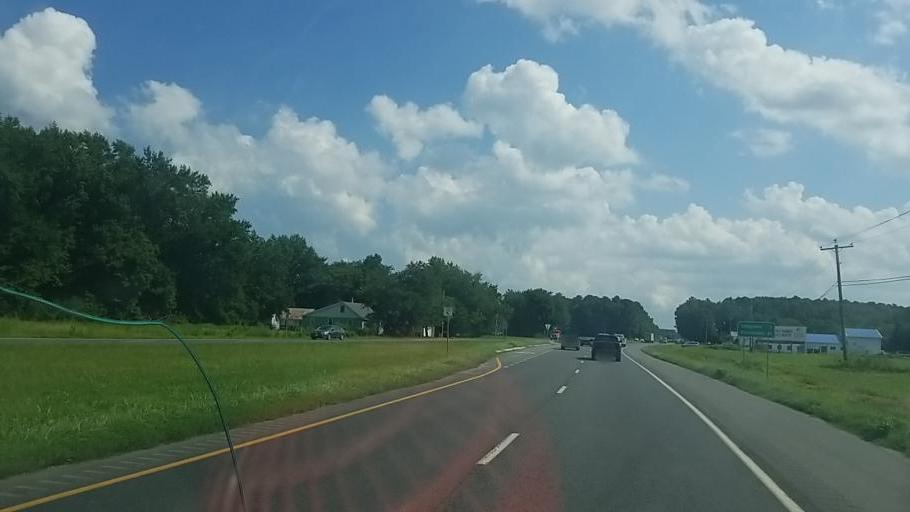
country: US
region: Delaware
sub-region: Sussex County
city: Selbyville
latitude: 38.5106
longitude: -75.2383
